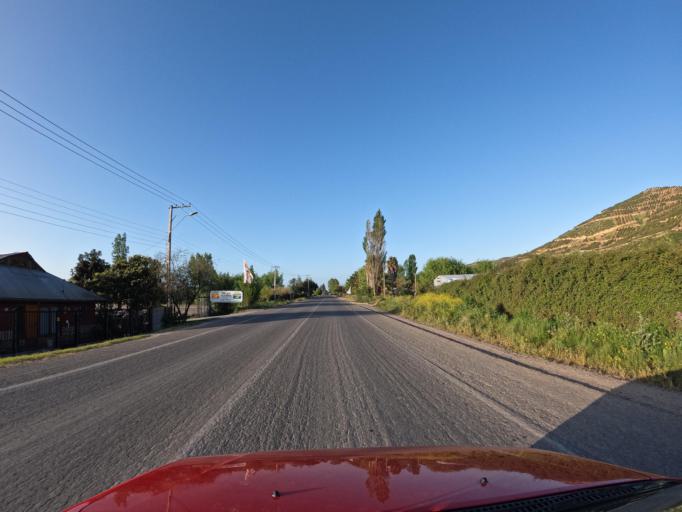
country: CL
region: O'Higgins
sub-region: Provincia de Colchagua
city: Santa Cruz
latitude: -34.3510
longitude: -71.4087
